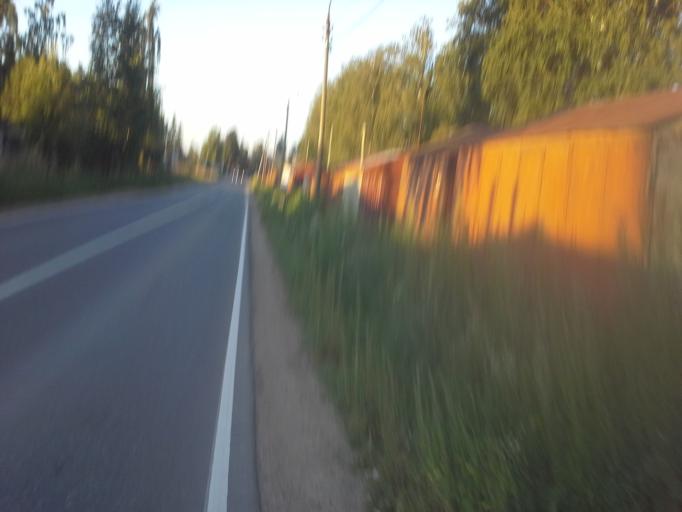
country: RU
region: Moskovskaya
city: Selyatino
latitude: 55.5230
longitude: 36.9659
